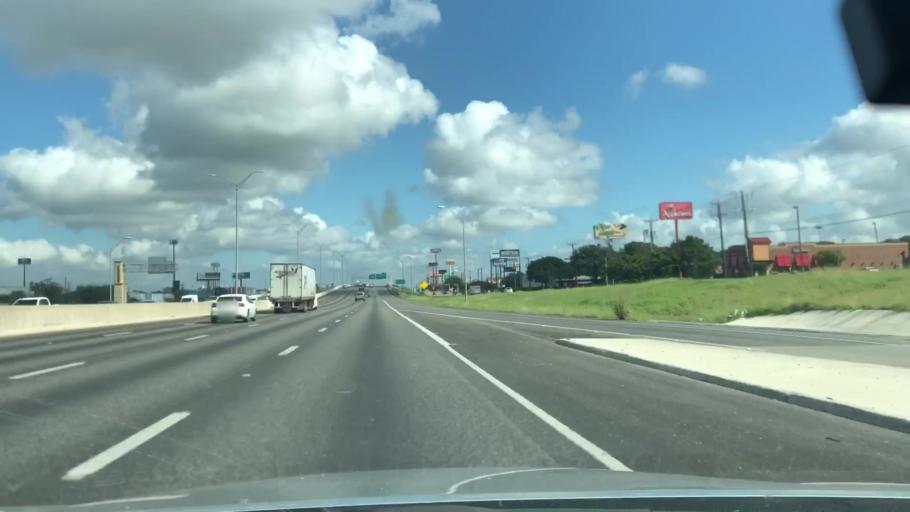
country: US
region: Texas
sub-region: Bexar County
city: Windcrest
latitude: 29.5056
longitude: -98.3986
